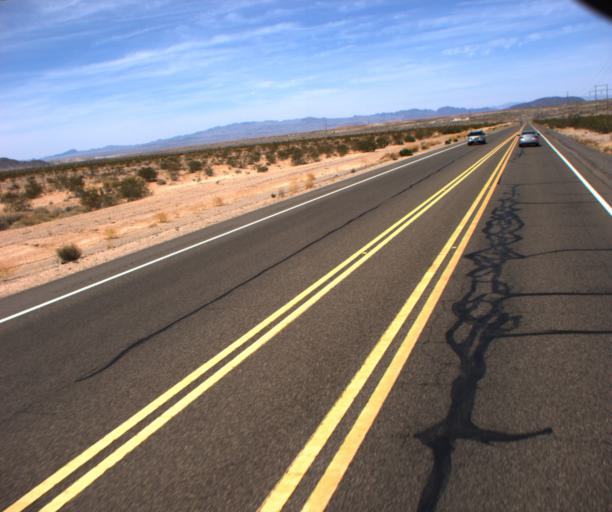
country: US
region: Arizona
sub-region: La Paz County
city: Parker
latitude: 33.9728
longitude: -114.2169
